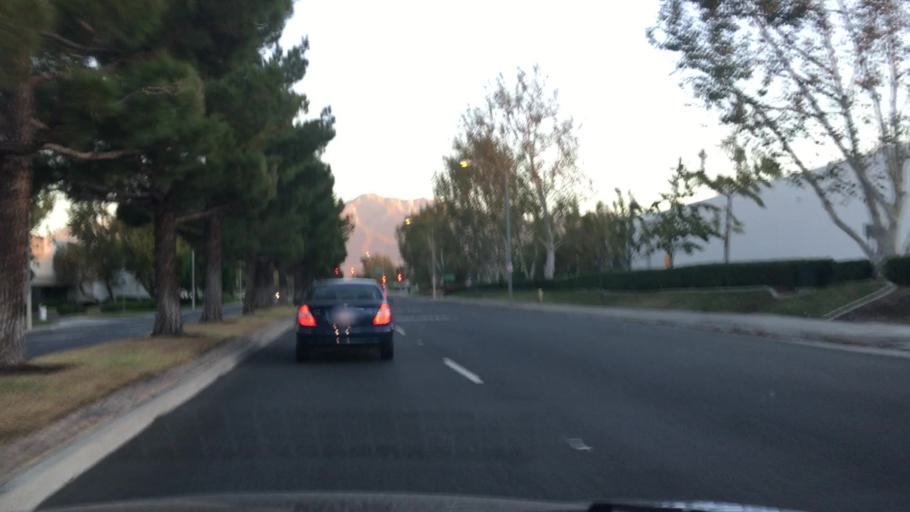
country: US
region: California
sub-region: San Bernardino County
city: Ontario
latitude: 34.0388
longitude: -117.5932
